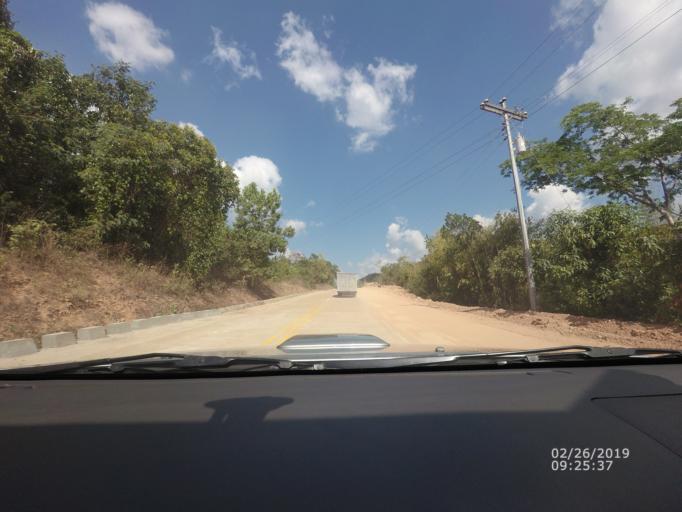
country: PH
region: Mimaropa
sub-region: Province of Palawan
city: Salvacion
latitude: 12.0344
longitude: 120.0388
